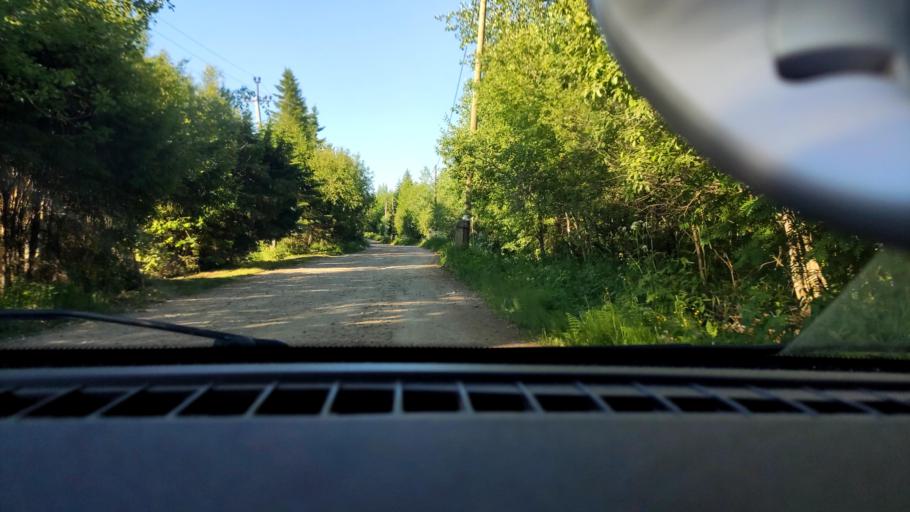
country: RU
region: Perm
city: Polazna
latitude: 58.2912
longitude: 56.1384
